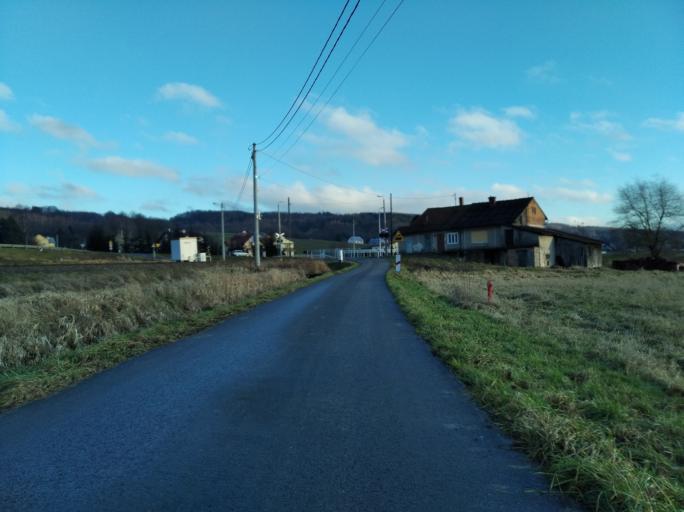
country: PL
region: Subcarpathian Voivodeship
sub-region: Powiat strzyzowski
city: Czudec
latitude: 49.9248
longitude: 21.8184
